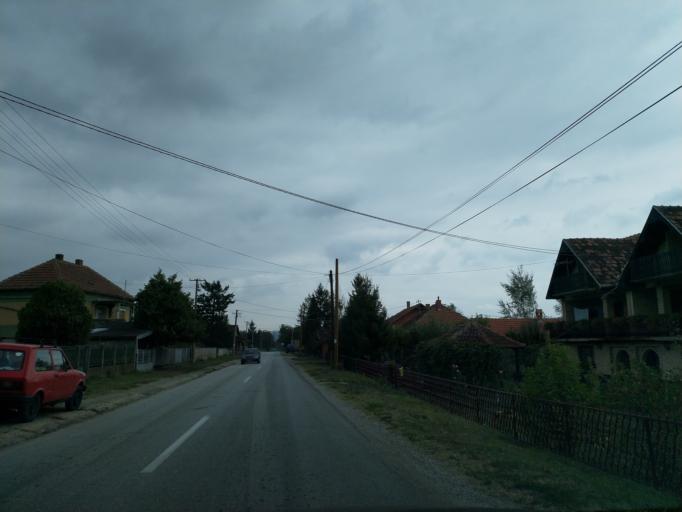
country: RS
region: Central Serbia
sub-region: Sumadijski Okrug
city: Batocina
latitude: 44.0788
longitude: 21.1814
